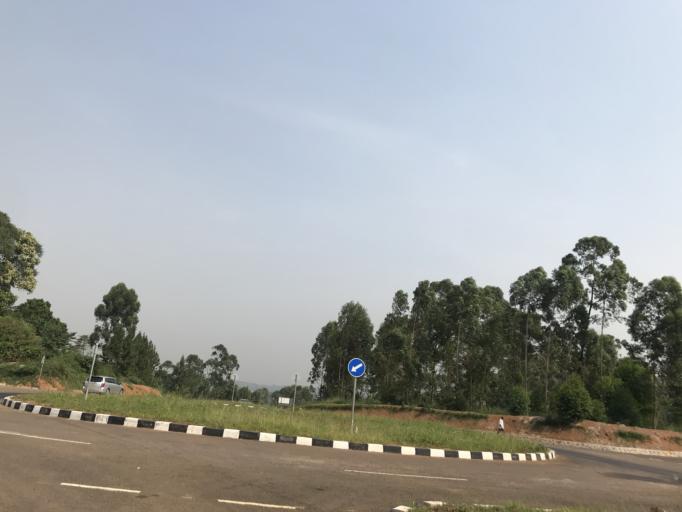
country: UG
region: Central Region
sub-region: Kalungu District
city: Kalungu
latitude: -0.2289
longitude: 31.7351
